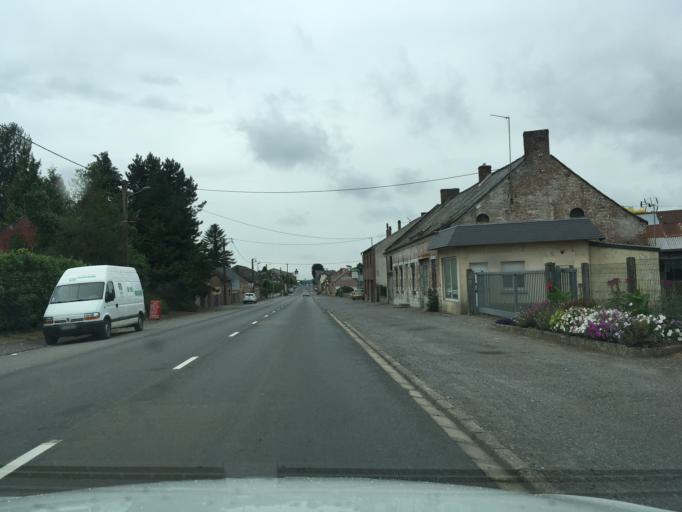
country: FR
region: Picardie
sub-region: Departement de l'Aisne
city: Buironfosse
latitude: 49.9649
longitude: 3.8394
